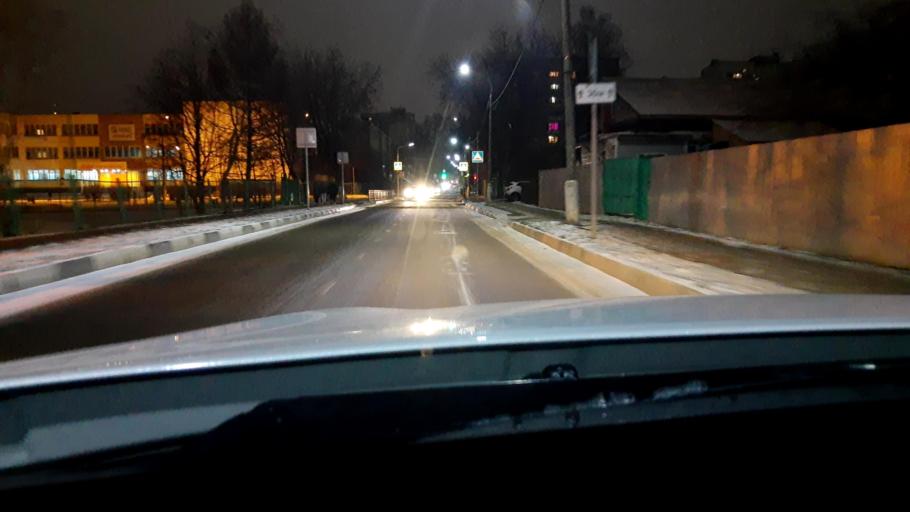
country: RU
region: Moskovskaya
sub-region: Podol'skiy Rayon
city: Podol'sk
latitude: 55.4344
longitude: 37.5391
